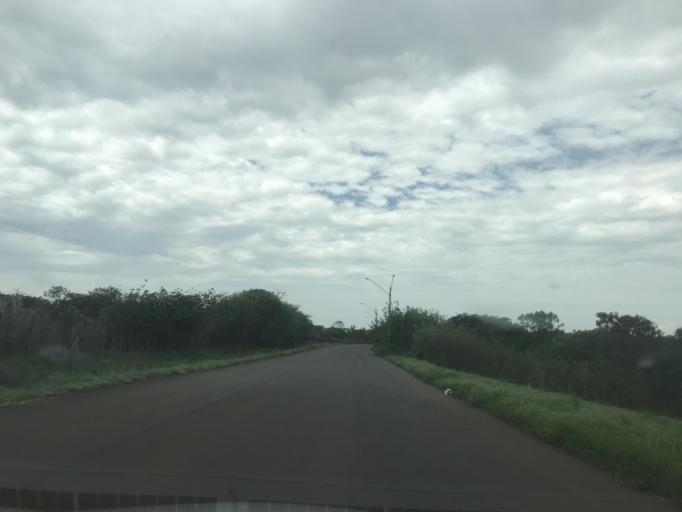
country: BR
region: Goias
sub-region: Luziania
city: Luziania
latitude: -16.2611
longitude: -47.9754
